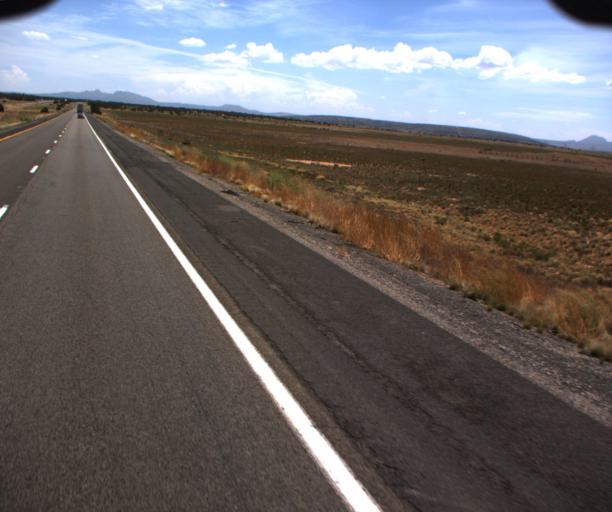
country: US
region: Arizona
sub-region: Mohave County
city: Peach Springs
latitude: 35.3105
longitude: -112.9780
